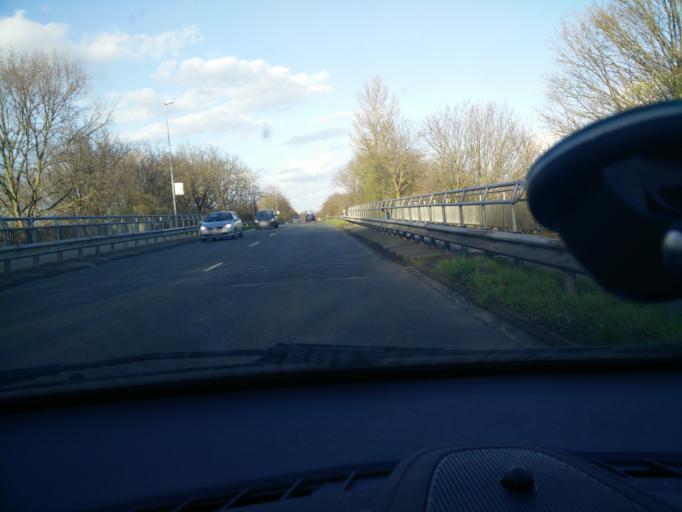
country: DE
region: North Rhine-Westphalia
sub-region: Regierungsbezirk Dusseldorf
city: Wesel
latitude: 51.6718
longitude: 6.6199
